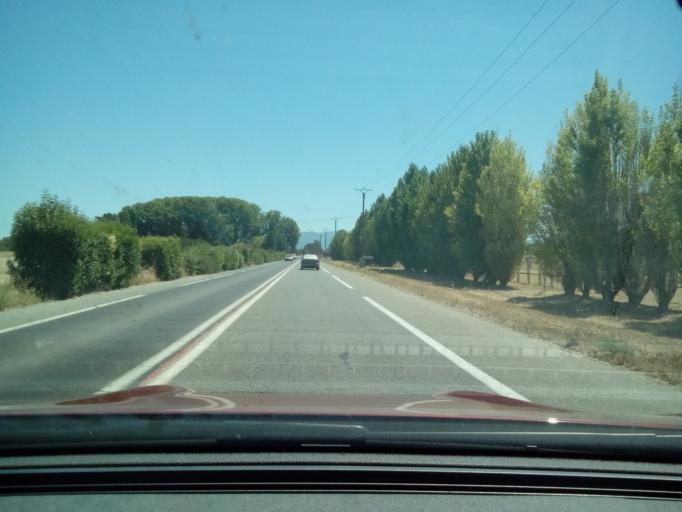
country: FR
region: Provence-Alpes-Cote d'Azur
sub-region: Departement des Bouches-du-Rhone
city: Chateauneuf-le-Rouge
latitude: 43.4714
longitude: 5.5865
